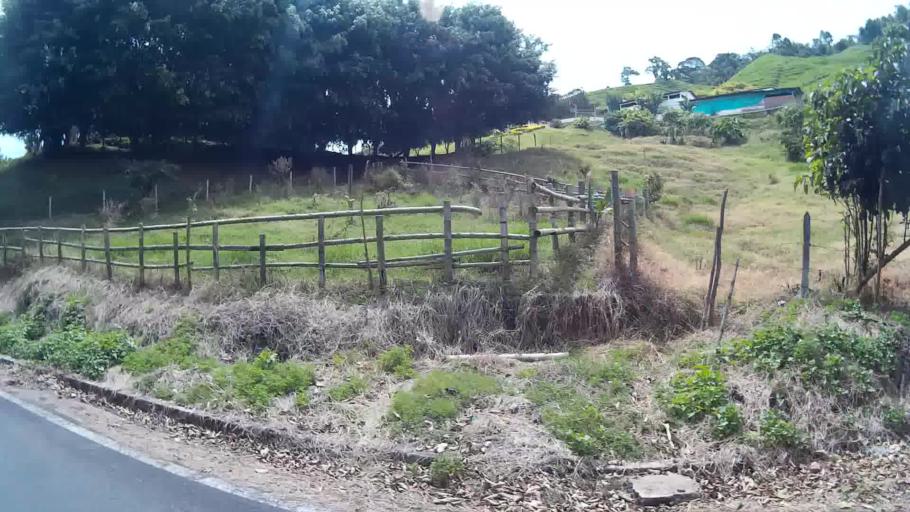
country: CO
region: Risaralda
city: Marsella
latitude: 4.8937
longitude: -75.7461
